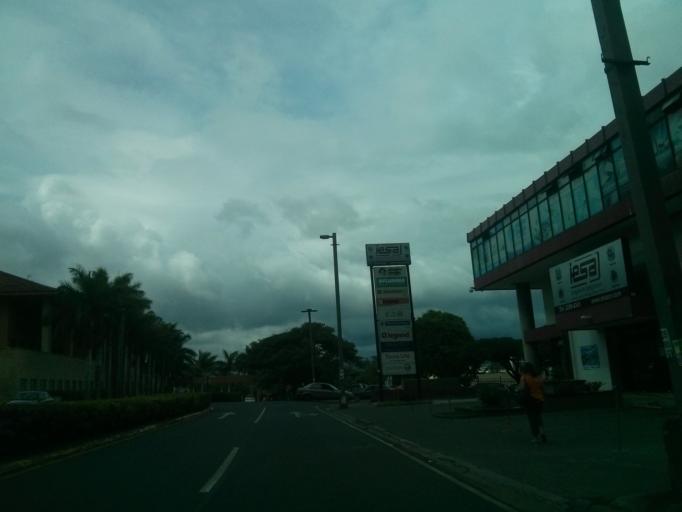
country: CR
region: San Jose
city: San Rafael
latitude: 9.9432
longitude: -84.1526
